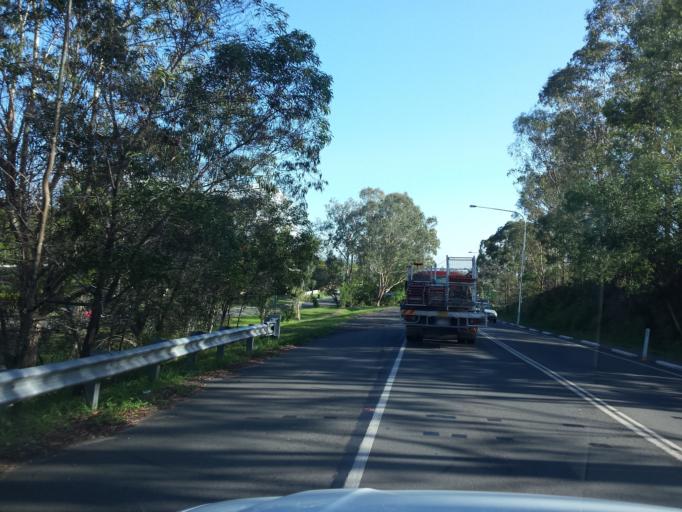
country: AU
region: Queensland
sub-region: Logan
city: Windaroo
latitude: -27.7254
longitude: 153.1935
